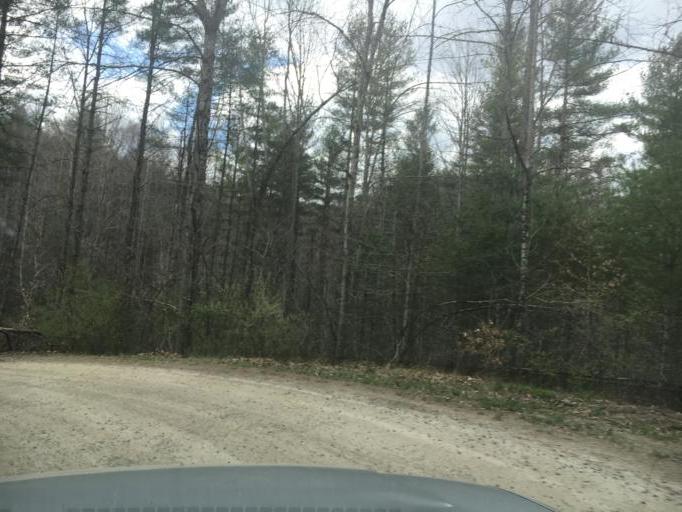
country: US
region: North Carolina
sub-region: Haywood County
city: Cove Creek
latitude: 35.6697
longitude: -83.0289
